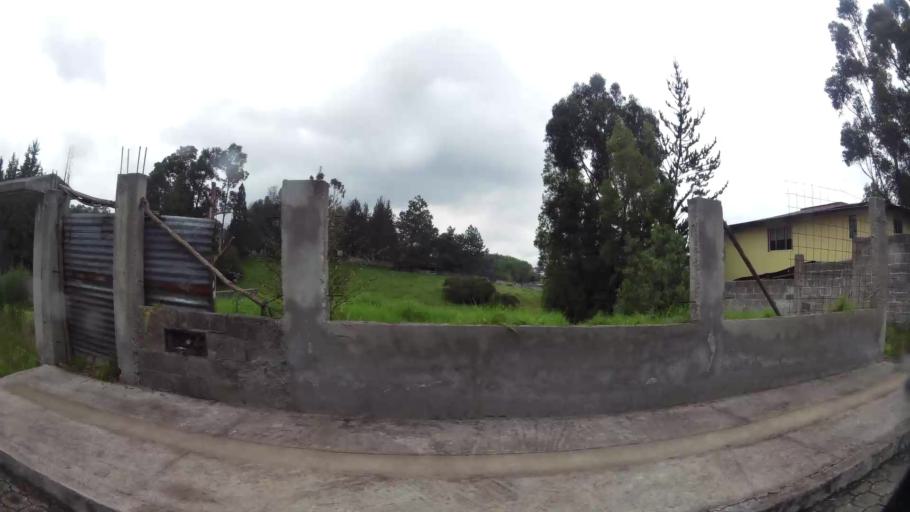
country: EC
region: Pichincha
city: Sangolqui
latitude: -0.3221
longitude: -78.4369
